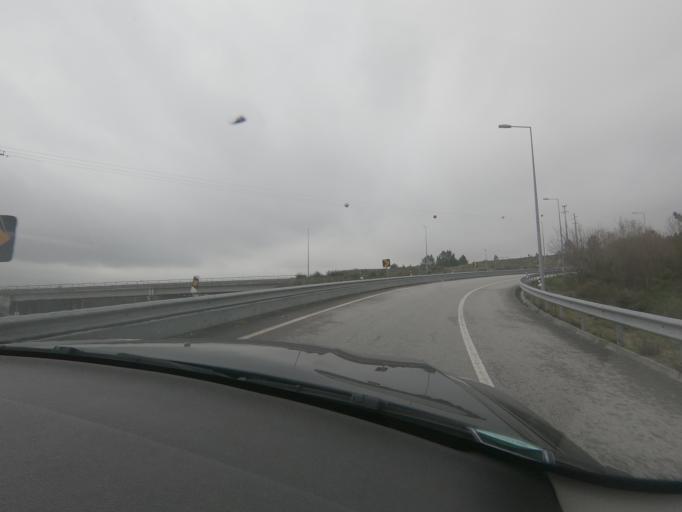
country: PT
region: Viseu
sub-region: Viseu
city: Abraveses
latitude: 40.6726
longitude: -7.9710
